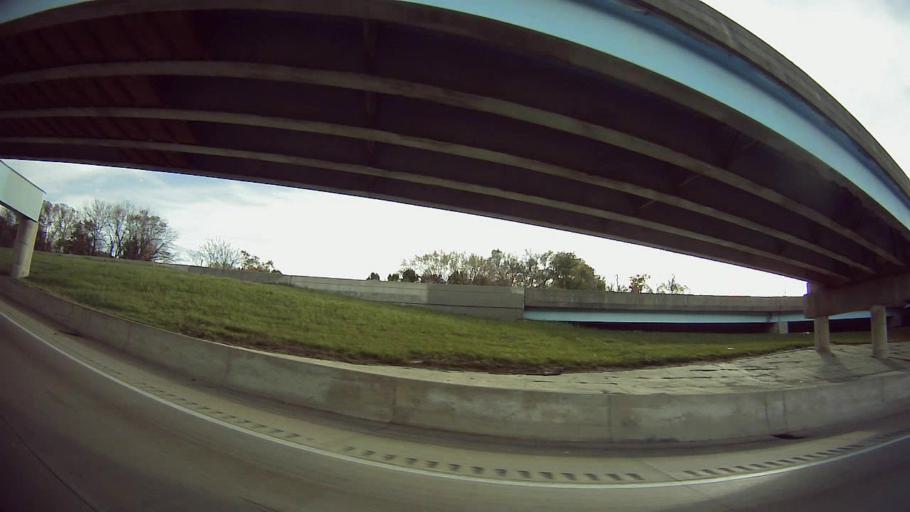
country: US
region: Michigan
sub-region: Wayne County
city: Dearborn
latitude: 42.3783
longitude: -83.2116
